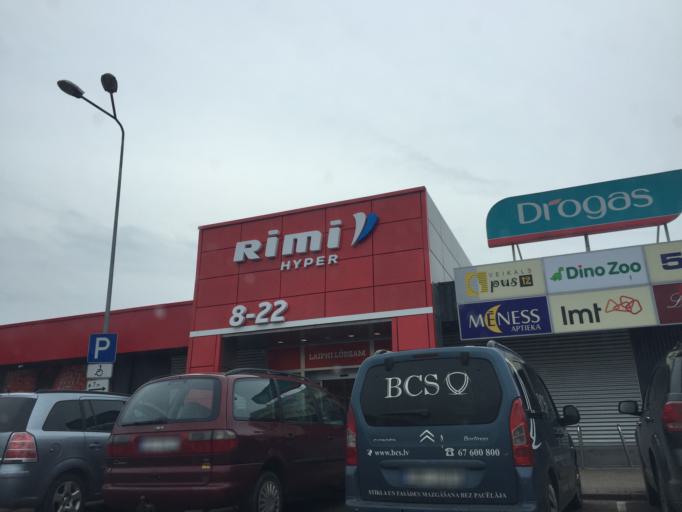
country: LV
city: Tireli
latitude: 56.9609
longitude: 23.6161
